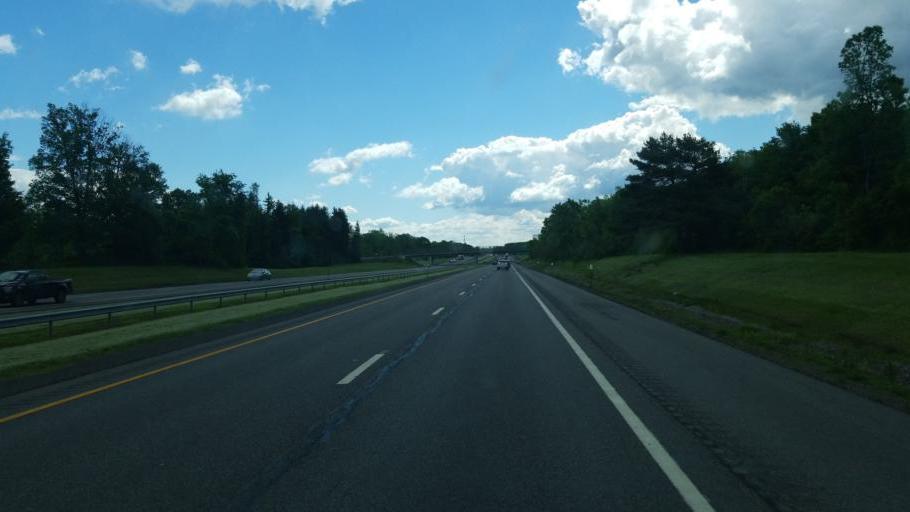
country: US
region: New York
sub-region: Madison County
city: Canastota
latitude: 43.0917
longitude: -75.7811
